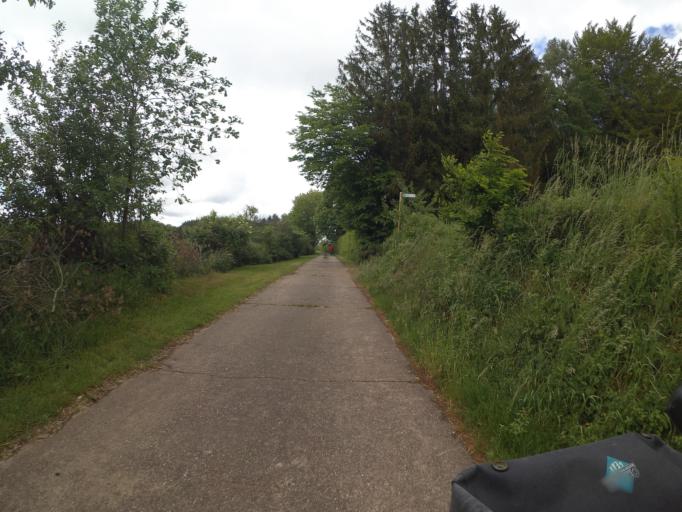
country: DE
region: Rheinland-Pfalz
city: Trulben
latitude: 49.1337
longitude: 7.5581
